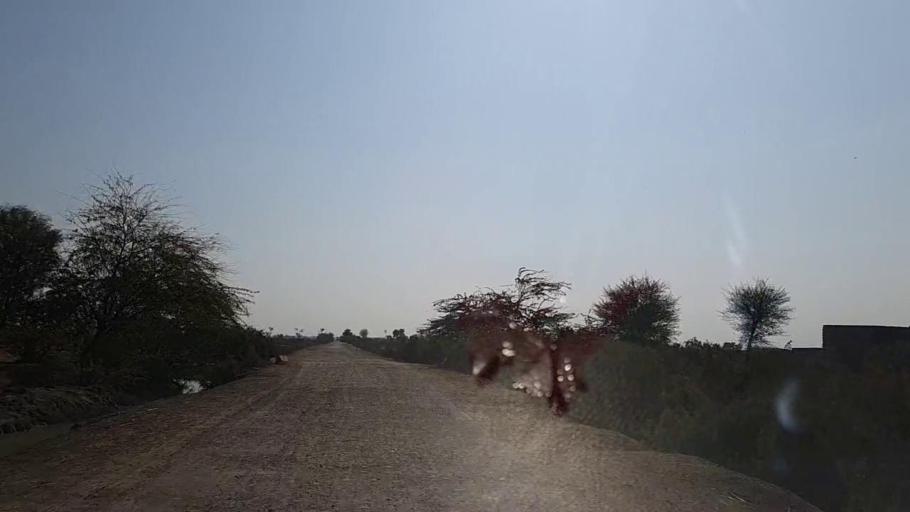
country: PK
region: Sindh
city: Sanghar
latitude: 26.0027
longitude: 69.0565
